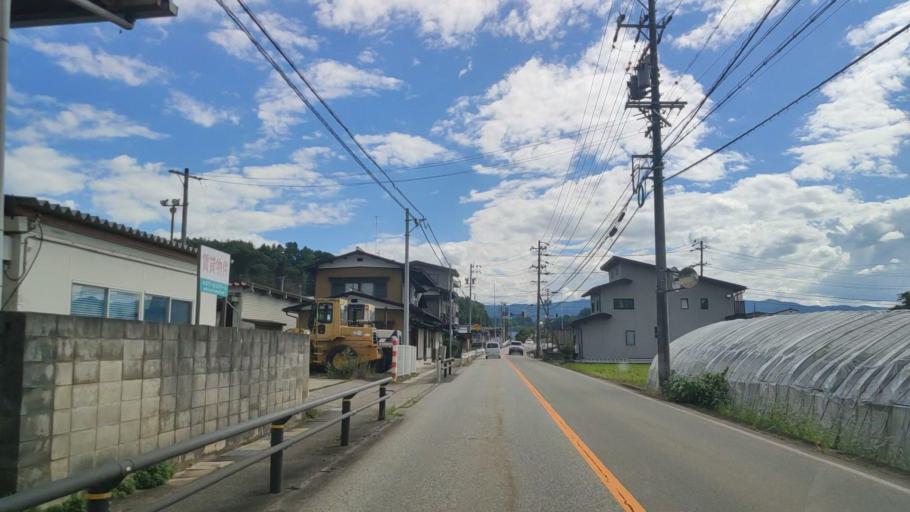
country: JP
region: Gifu
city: Takayama
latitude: 36.1632
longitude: 137.2517
